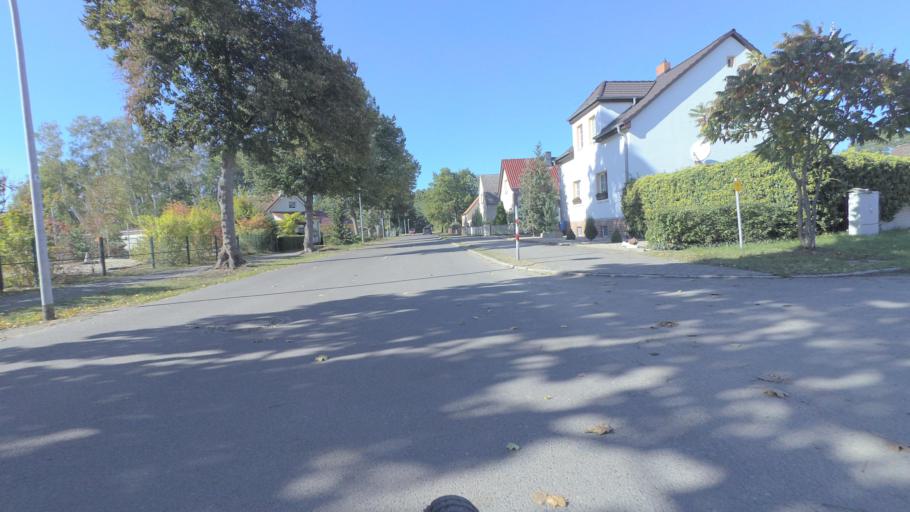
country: DE
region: Brandenburg
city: Sperenberg
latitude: 52.1416
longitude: 13.3574
